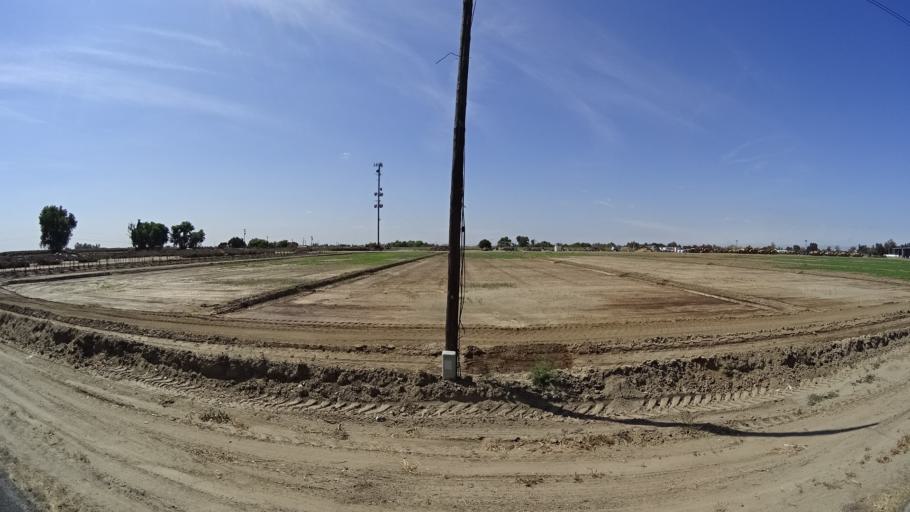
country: US
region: California
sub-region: Kings County
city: Lemoore
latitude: 36.2695
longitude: -119.7742
